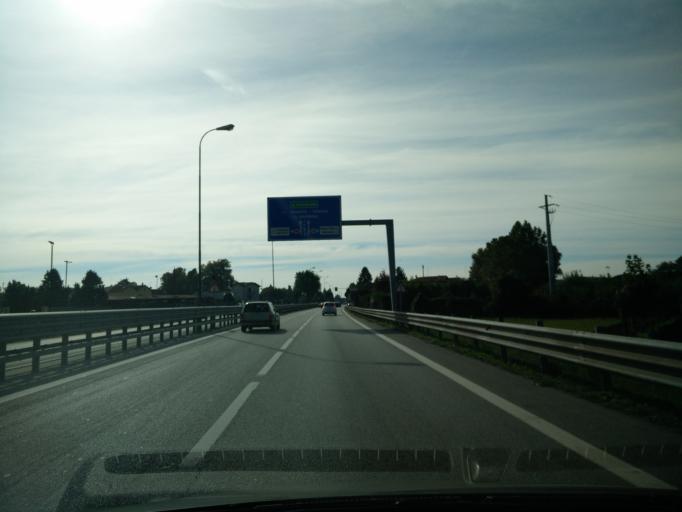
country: IT
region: Veneto
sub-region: Provincia di Venezia
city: Campalto
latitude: 45.4935
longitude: 12.2747
